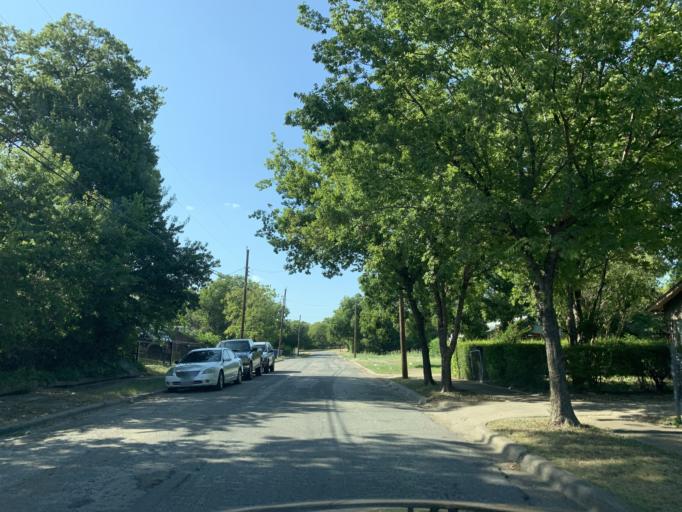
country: US
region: Texas
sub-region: Dallas County
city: Dallas
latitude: 32.7007
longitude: -96.7907
